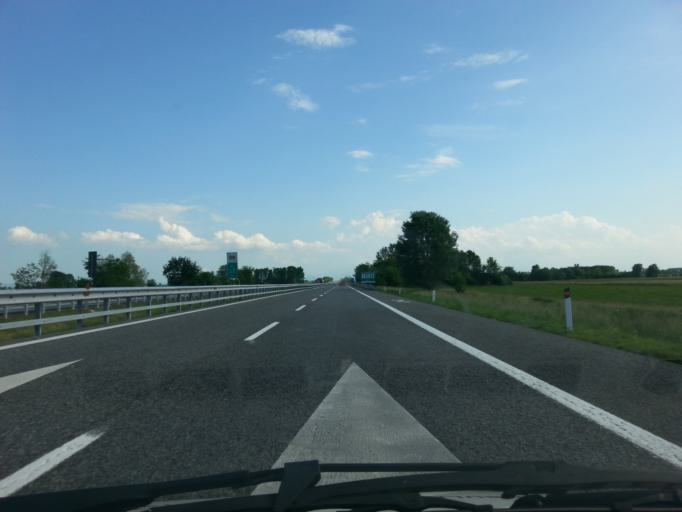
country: IT
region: Piedmont
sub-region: Provincia di Cuneo
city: Marene
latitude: 44.7117
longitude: 7.7608
